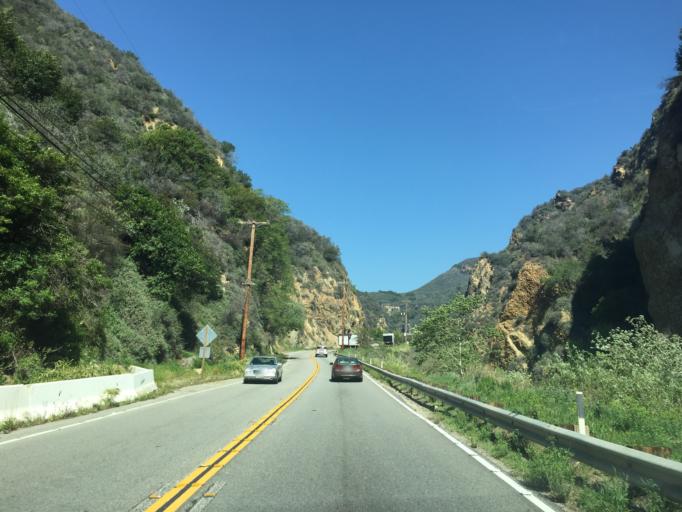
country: US
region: California
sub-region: Los Angeles County
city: Topanga
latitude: 34.0673
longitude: -118.5870
